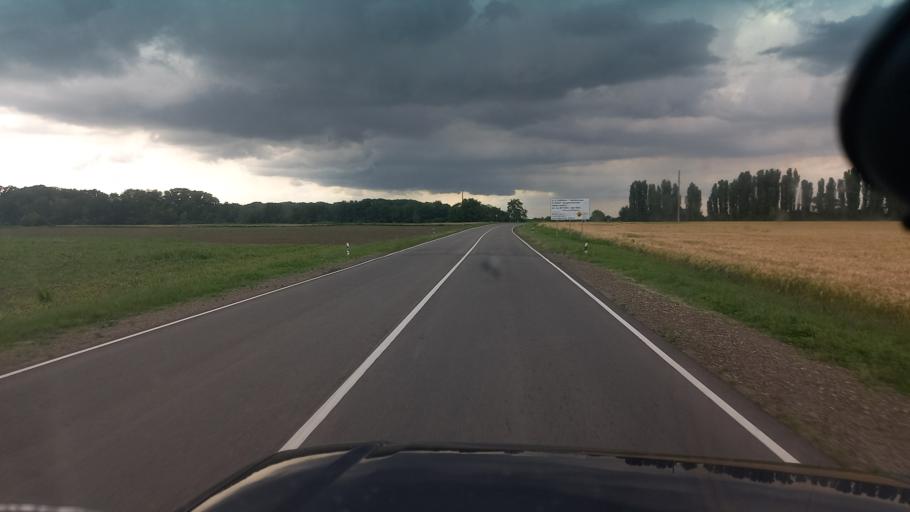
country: RU
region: Adygeya
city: Shovgenovskiy
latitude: 44.9986
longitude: 40.2880
